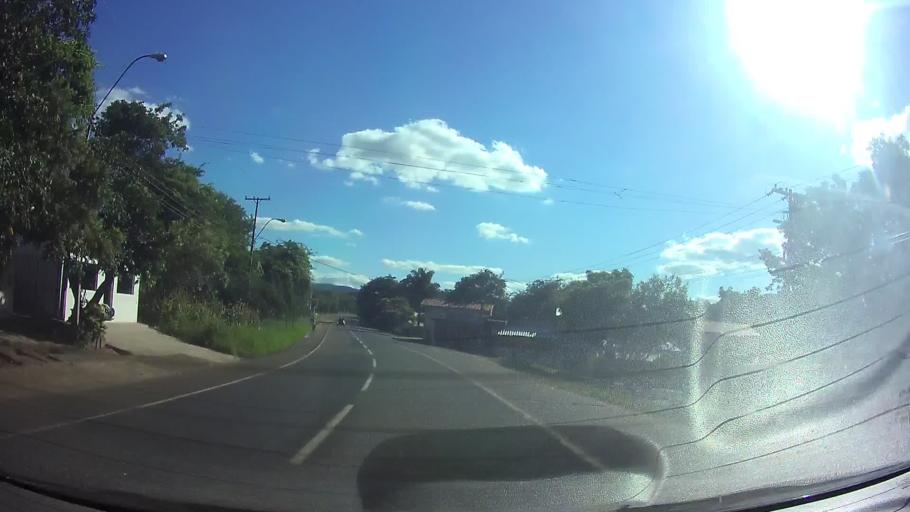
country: PY
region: Cordillera
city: Caacupe
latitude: -25.3854
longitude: -57.1325
